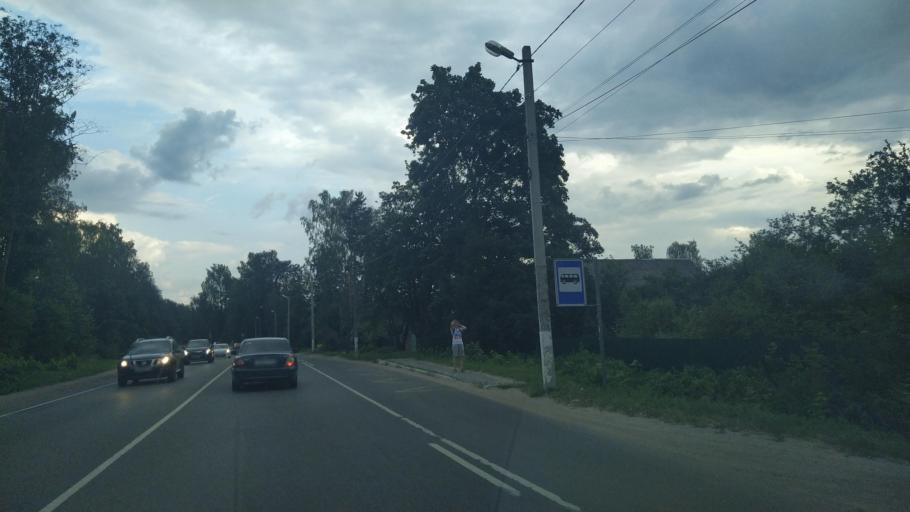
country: RU
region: Leningrad
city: Toksovo
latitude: 60.1483
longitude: 30.5230
